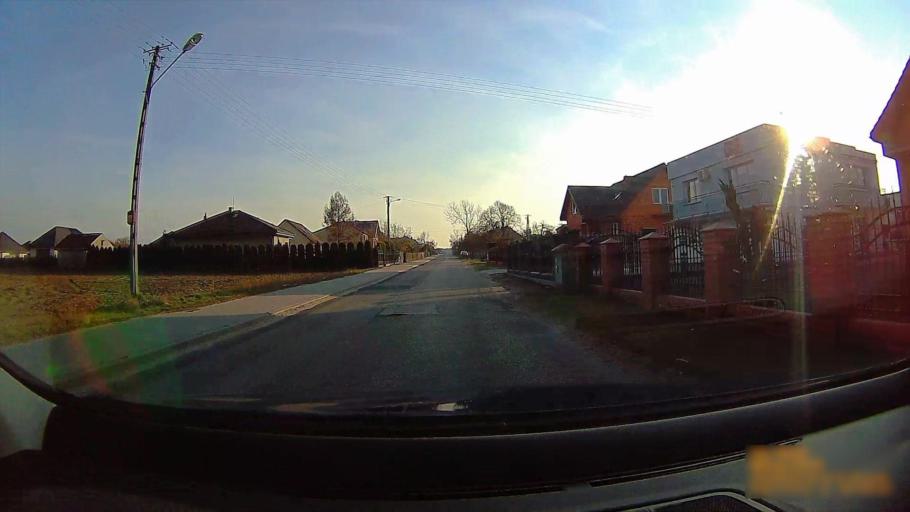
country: PL
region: Greater Poland Voivodeship
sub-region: Konin
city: Konin
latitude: 52.1879
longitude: 18.3018
